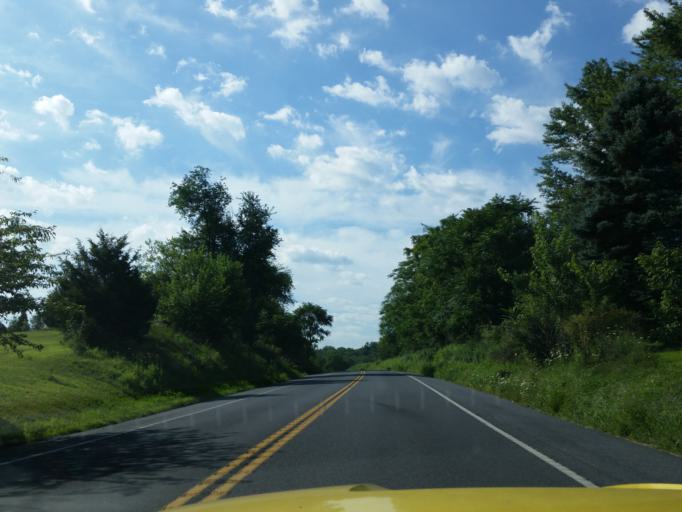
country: US
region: Pennsylvania
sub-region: Lebanon County
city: Sand Hill
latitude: 40.3994
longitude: -76.4189
